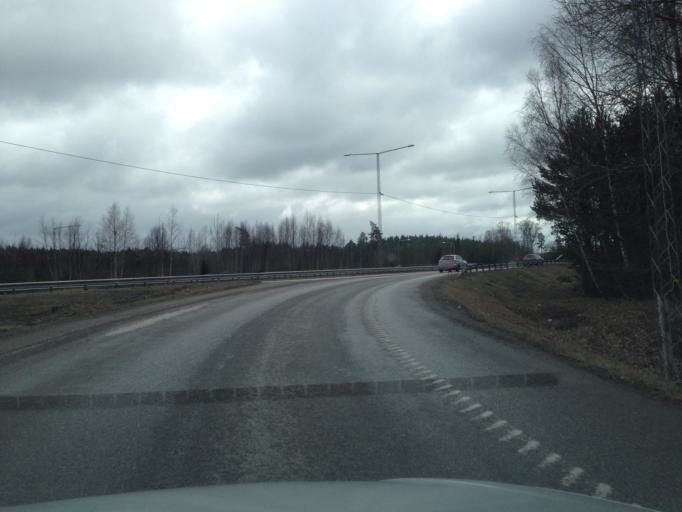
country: SE
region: Stockholm
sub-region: Vallentuna Kommun
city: Vallentuna
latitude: 59.4982
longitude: 18.1644
